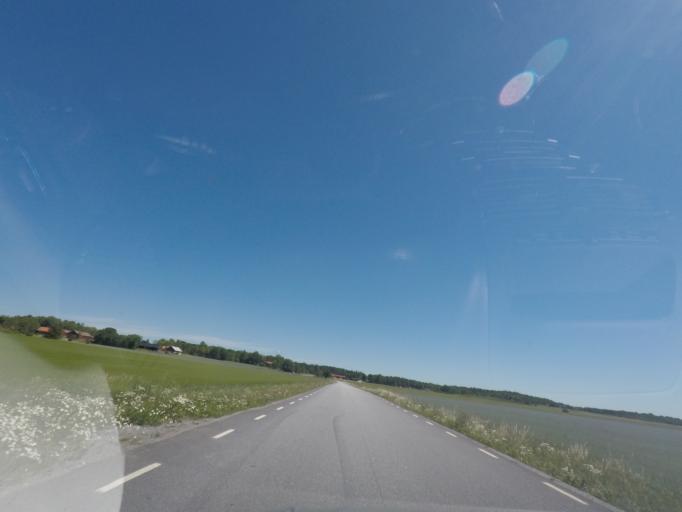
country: SE
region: Uppsala
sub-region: Enkopings Kommun
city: Enkoping
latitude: 59.7111
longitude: 17.0591
